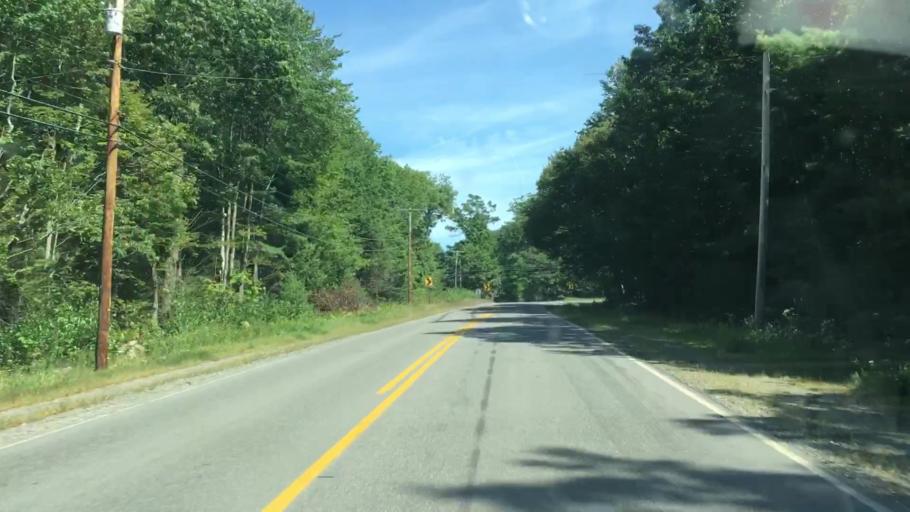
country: US
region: Maine
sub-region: Penobscot County
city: Bradford
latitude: 45.1771
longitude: -68.8560
